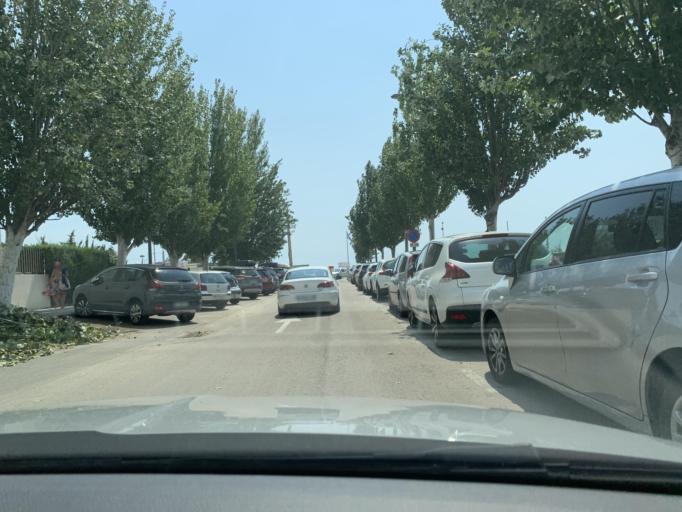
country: ES
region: Catalonia
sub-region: Provincia de Tarragona
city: Altafulla
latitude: 41.1293
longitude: 1.3460
